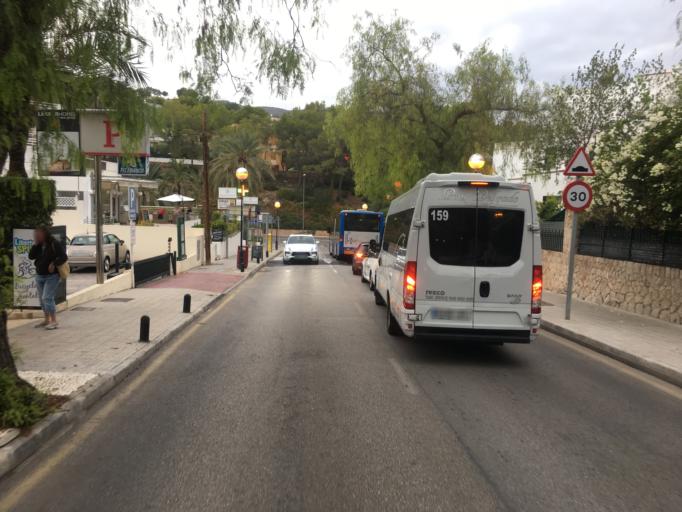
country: ES
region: Balearic Islands
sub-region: Illes Balears
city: Palma
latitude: 39.5443
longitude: 2.5953
